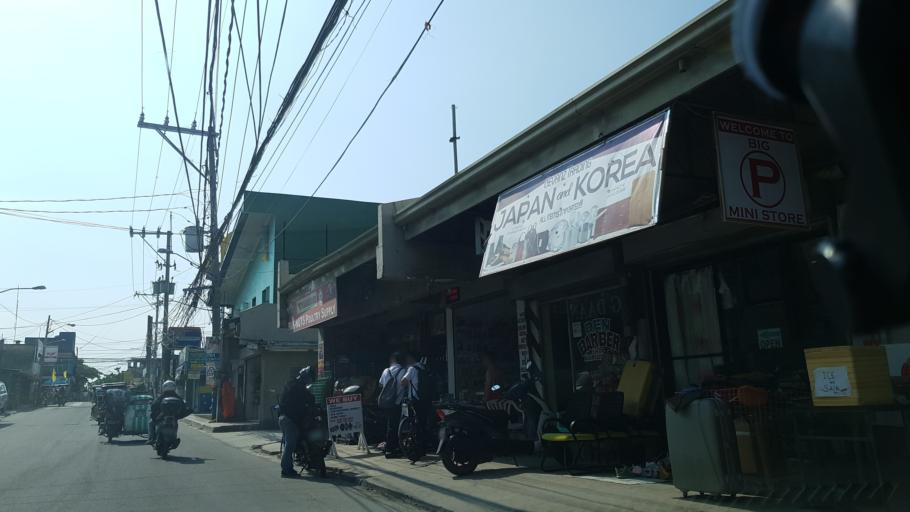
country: PH
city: Sambayanihan People's Village
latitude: 14.4918
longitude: 121.0157
